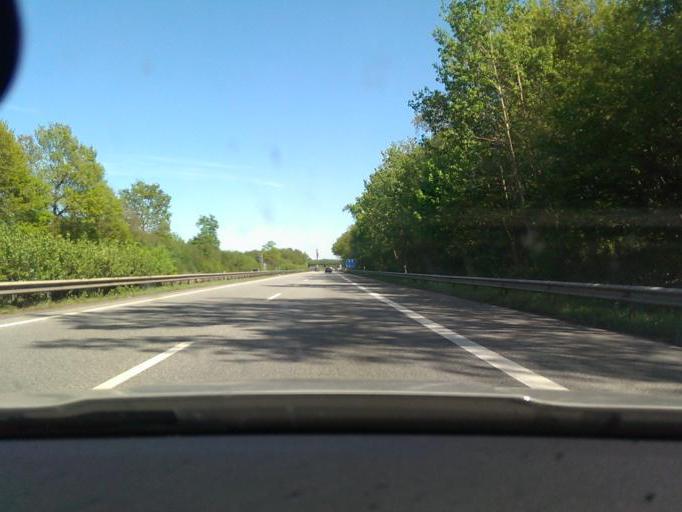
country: DE
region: Lower Saxony
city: Achim
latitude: 53.0219
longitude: 9.0456
